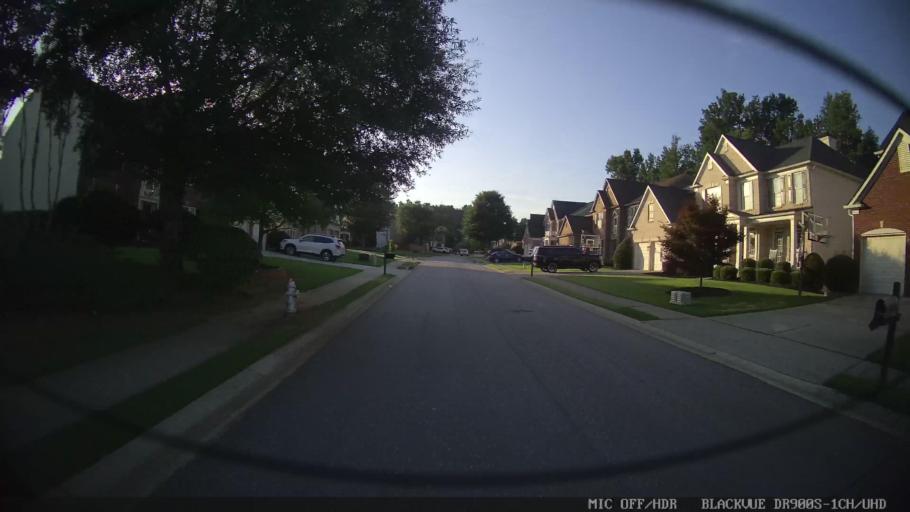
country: US
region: Georgia
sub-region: Forsyth County
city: Cumming
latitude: 34.2160
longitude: -84.2318
